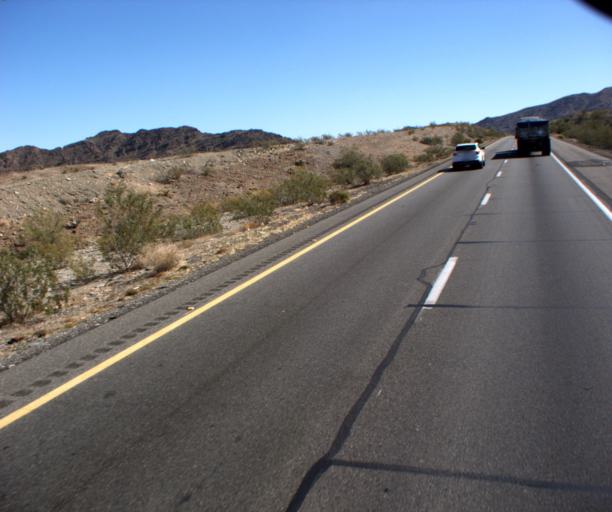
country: US
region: Arizona
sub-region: La Paz County
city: Ehrenberg
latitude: 33.6311
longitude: -114.4072
